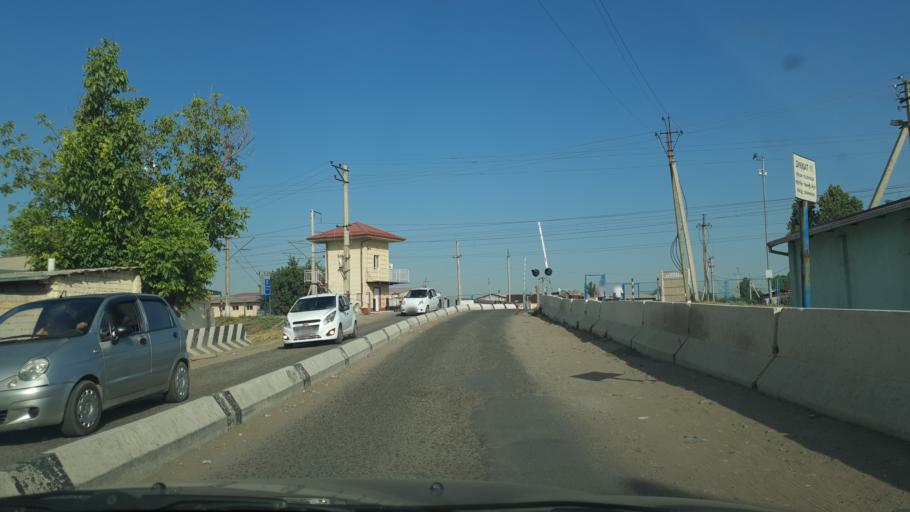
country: UZ
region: Toshkent
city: Urtaowul
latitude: 41.2009
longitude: 69.1562
